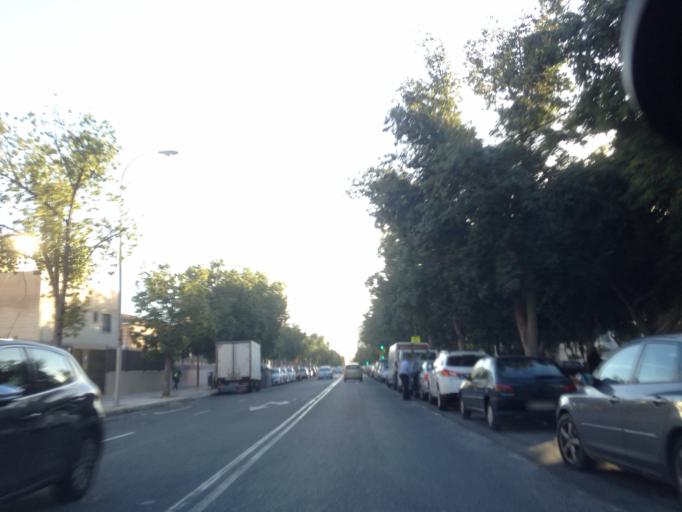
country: ES
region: Andalusia
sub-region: Provincia de Malaga
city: Malaga
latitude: 36.6969
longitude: -4.4469
